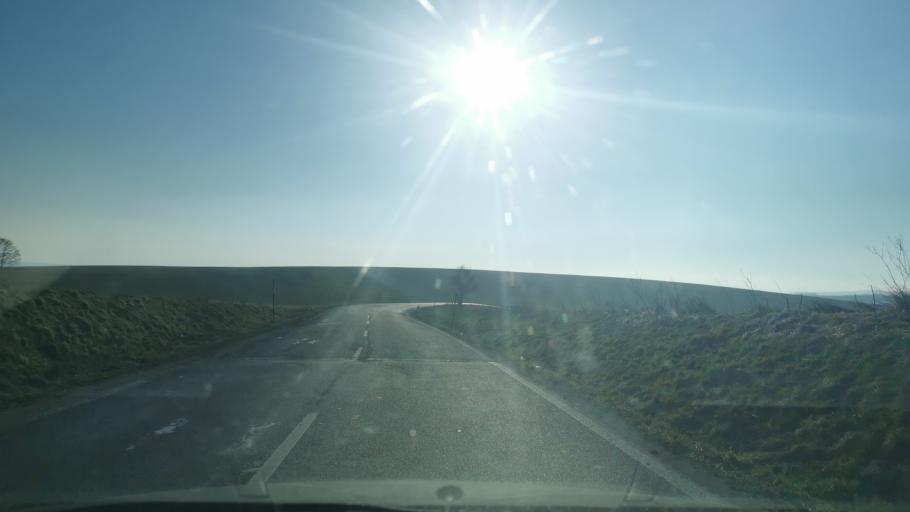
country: SK
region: Trnavsky
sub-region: Okres Senica
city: Senica
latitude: 48.7361
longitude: 17.3722
